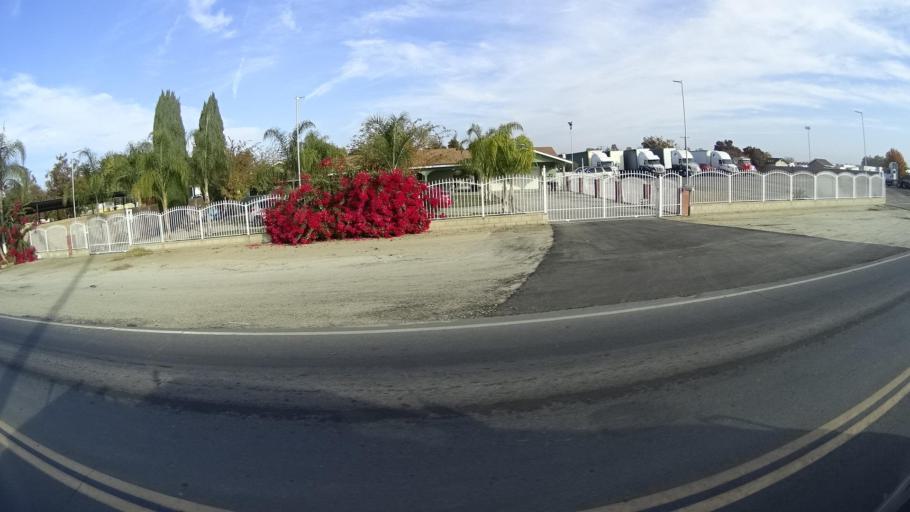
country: US
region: California
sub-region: Kern County
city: Delano
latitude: 35.7905
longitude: -119.2223
